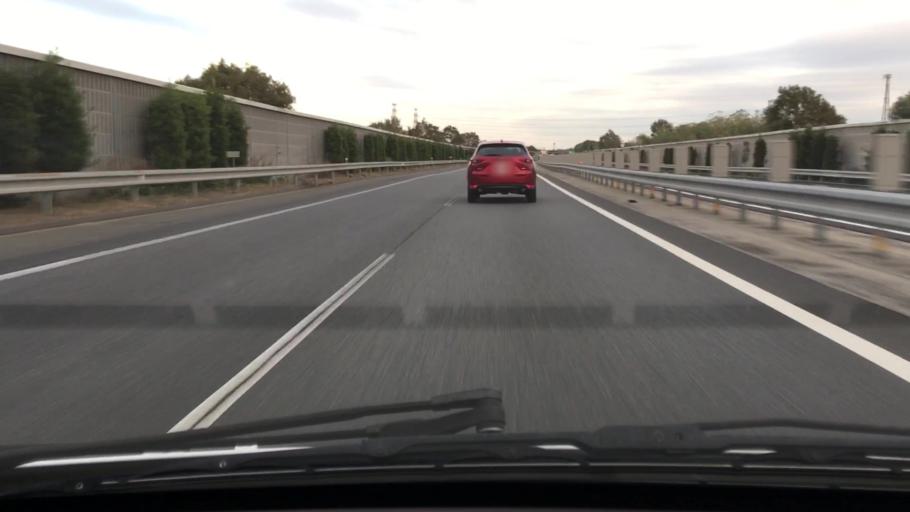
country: JP
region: Chiba
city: Ichihara
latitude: 35.5040
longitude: 140.1023
